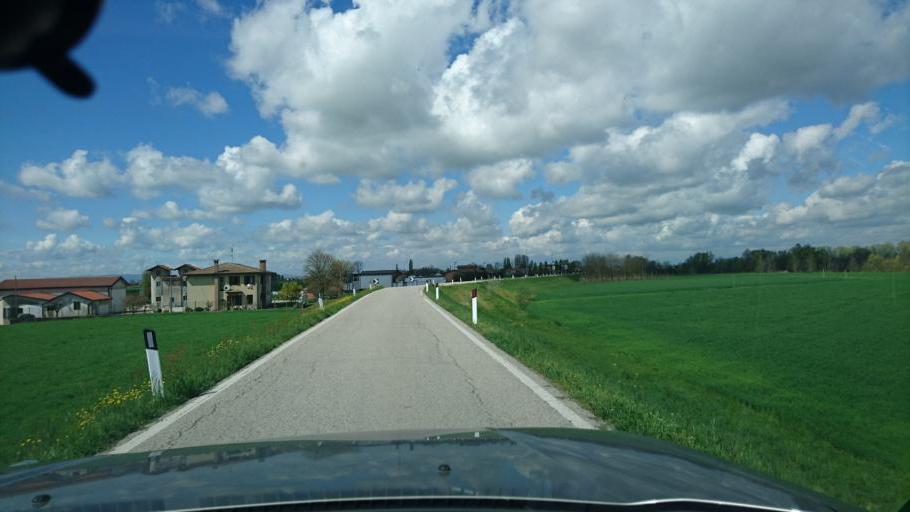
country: IT
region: Veneto
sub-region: Provincia di Padova
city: Curtarolo
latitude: 45.5162
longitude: 11.8252
